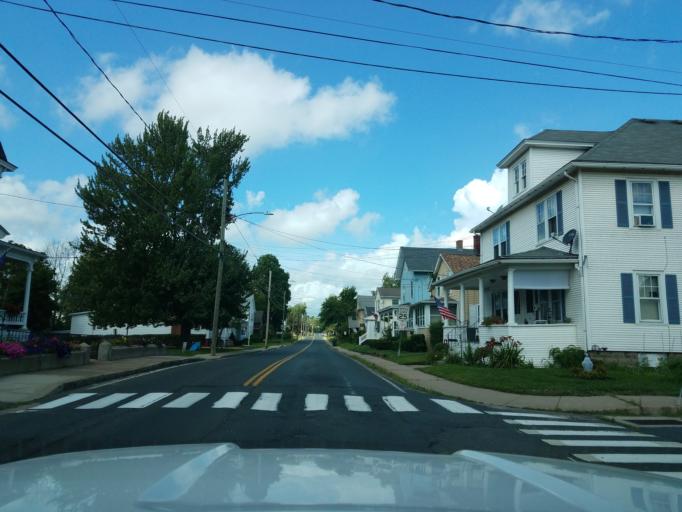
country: US
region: Connecticut
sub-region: Hartford County
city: Windsor Locks
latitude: 41.9307
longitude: -72.6299
